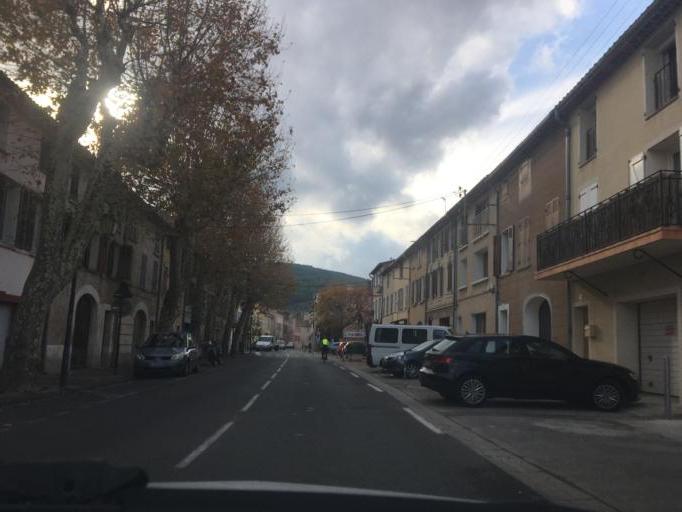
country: FR
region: Provence-Alpes-Cote d'Azur
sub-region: Departement du Var
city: Cuers
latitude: 43.2404
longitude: 6.0753
